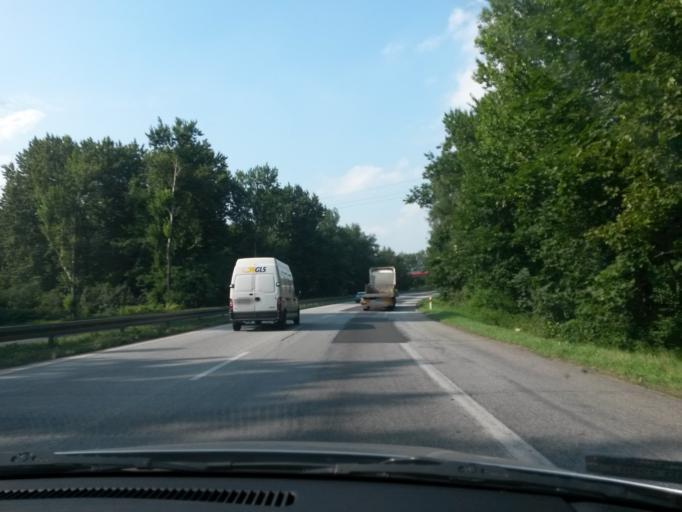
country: PL
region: Silesian Voivodeship
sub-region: Myslowice
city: Myslowice
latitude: 50.2404
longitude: 19.1702
